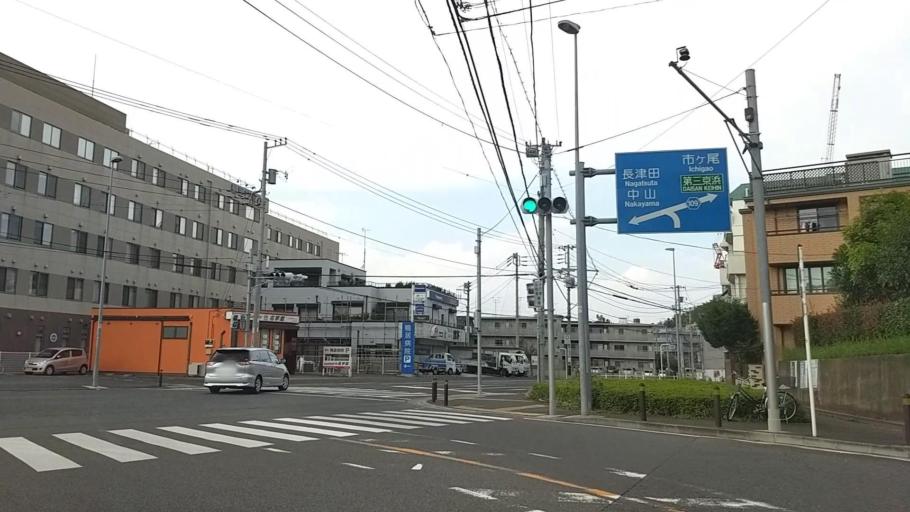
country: JP
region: Kanagawa
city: Yokohama
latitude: 35.5046
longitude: 139.5637
